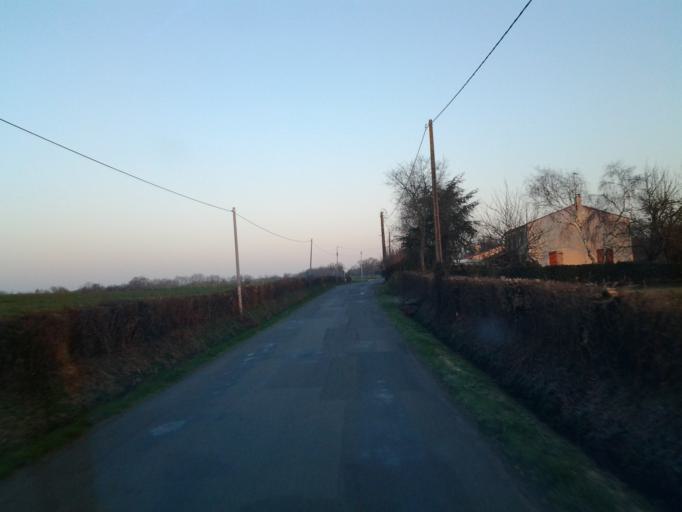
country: FR
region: Pays de la Loire
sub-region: Departement de la Vendee
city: La Chaize-le-Vicomte
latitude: 46.6624
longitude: -1.2425
